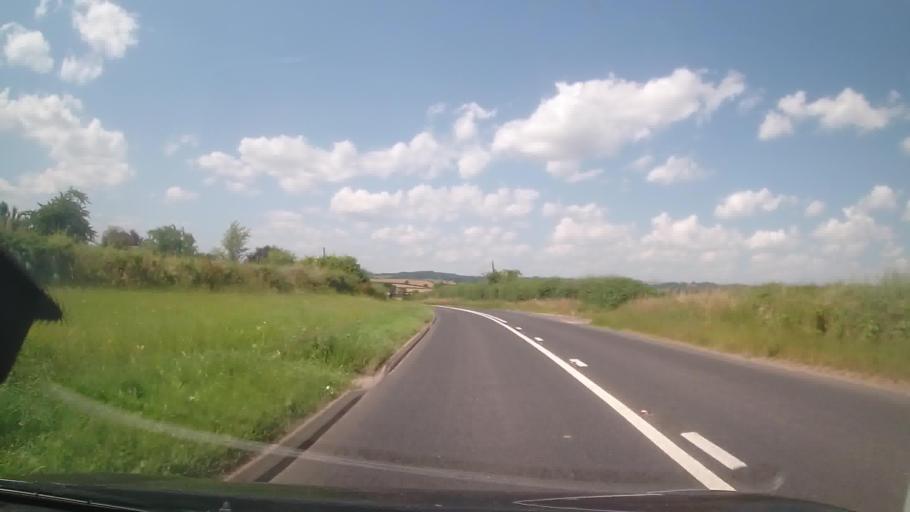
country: GB
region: England
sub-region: Herefordshire
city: Ocle Pychard
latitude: 52.1229
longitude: -2.5972
